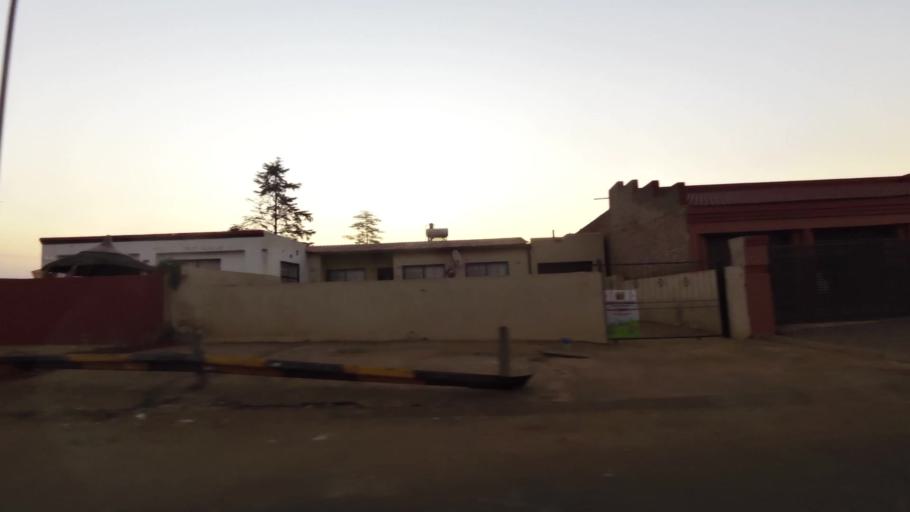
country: ZA
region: Gauteng
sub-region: City of Johannesburg Metropolitan Municipality
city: Soweto
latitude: -26.2935
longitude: 27.8710
